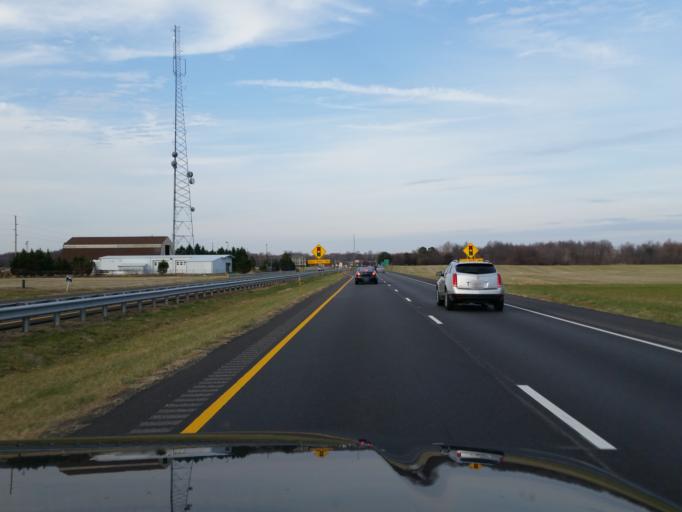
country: US
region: Maryland
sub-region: Queen Anne's County
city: Centreville
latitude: 38.9329
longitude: -76.0624
